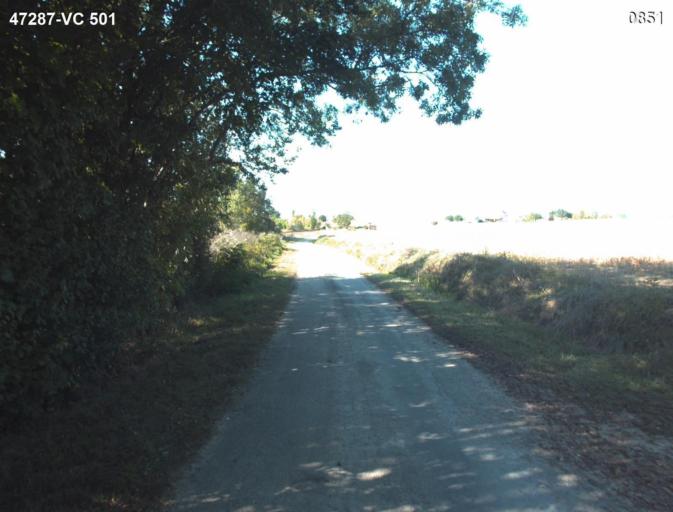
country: FR
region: Aquitaine
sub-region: Departement du Lot-et-Garonne
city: Laplume
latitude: 44.1130
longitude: 0.4610
